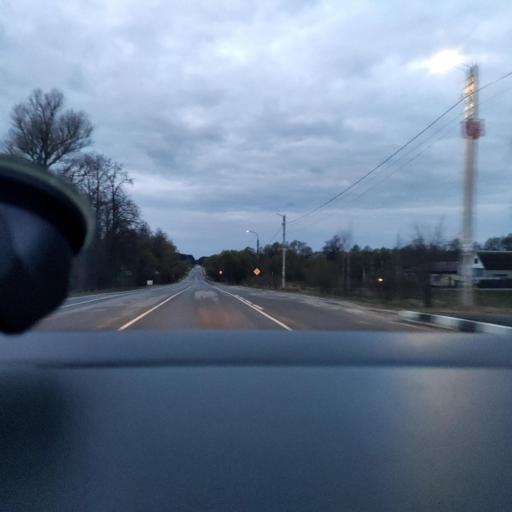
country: RU
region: Moskovskaya
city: Krasnyy Tkach
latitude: 55.4261
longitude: 39.1926
